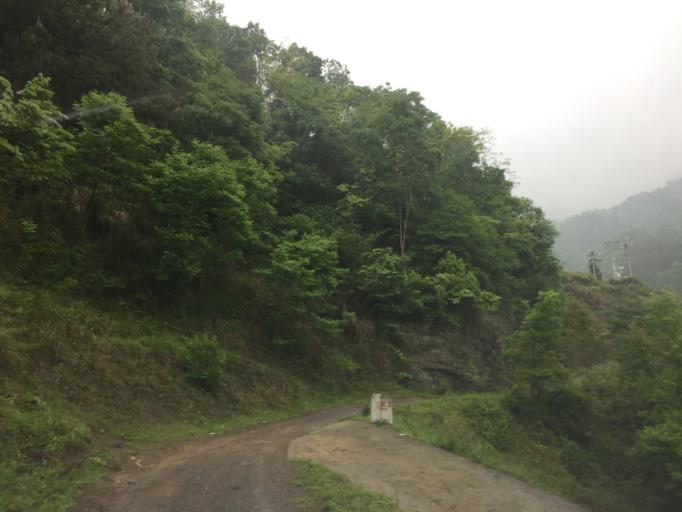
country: CN
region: Guizhou Sheng
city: Donghua
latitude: 28.0455
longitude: 108.1060
